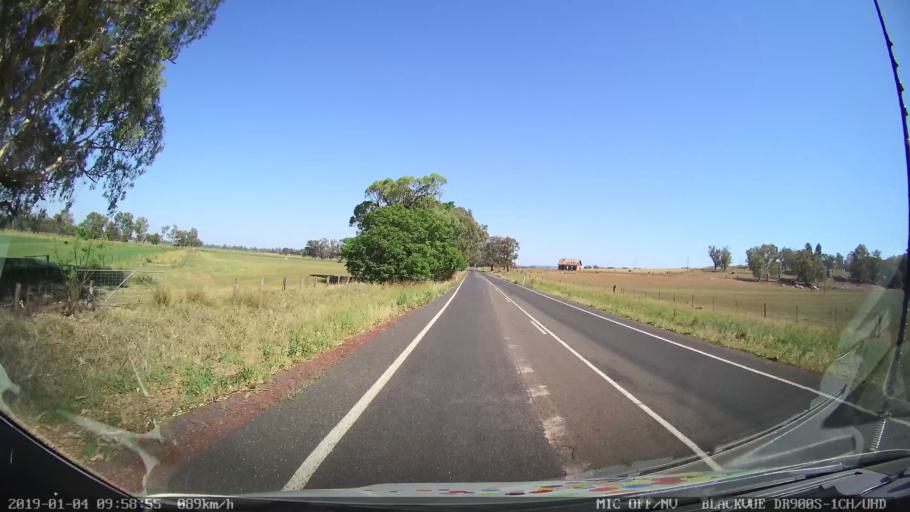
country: AU
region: New South Wales
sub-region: Cabonne
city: Canowindra
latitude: -33.5134
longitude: 148.3904
